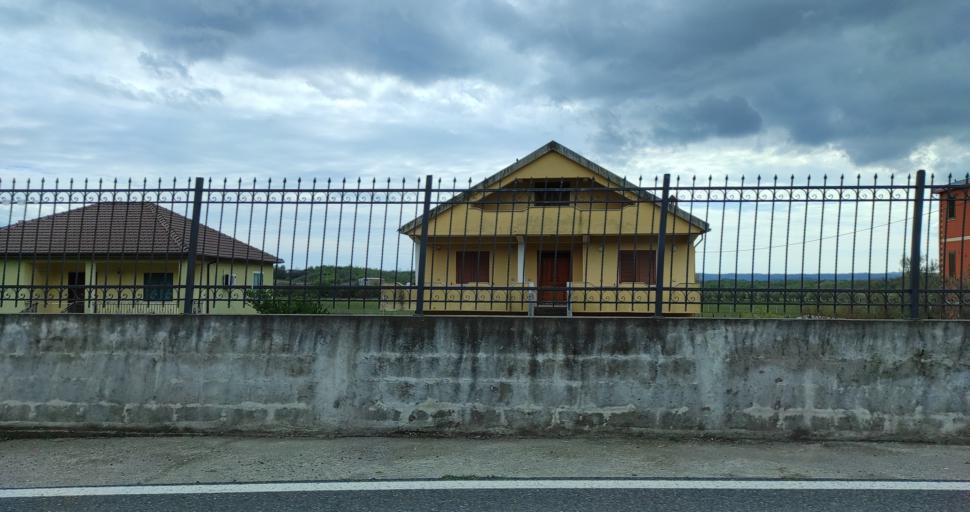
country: AL
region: Shkoder
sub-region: Rrethi i Shkodres
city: Dajc
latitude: 42.0180
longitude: 19.3856
